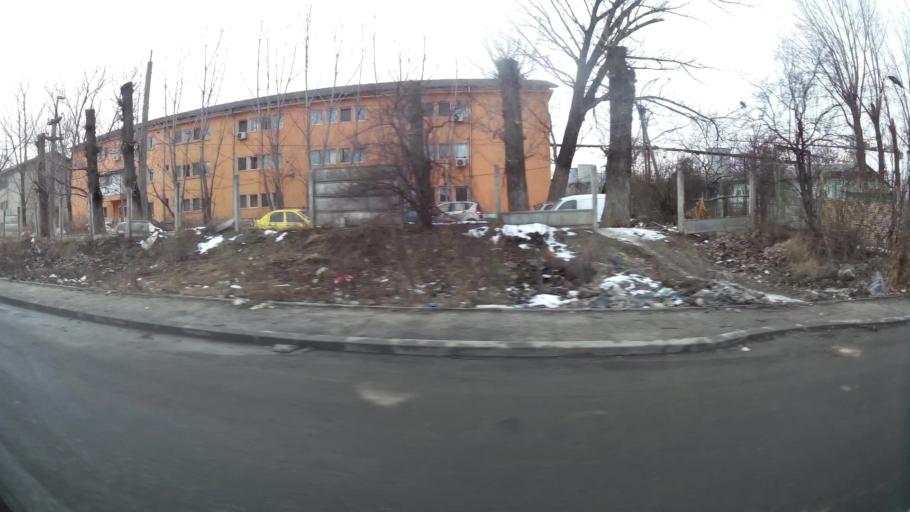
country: RO
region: Ilfov
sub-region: Comuna Popesti-Leordeni
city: Popesti-Leordeni
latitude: 44.4032
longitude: 26.1618
